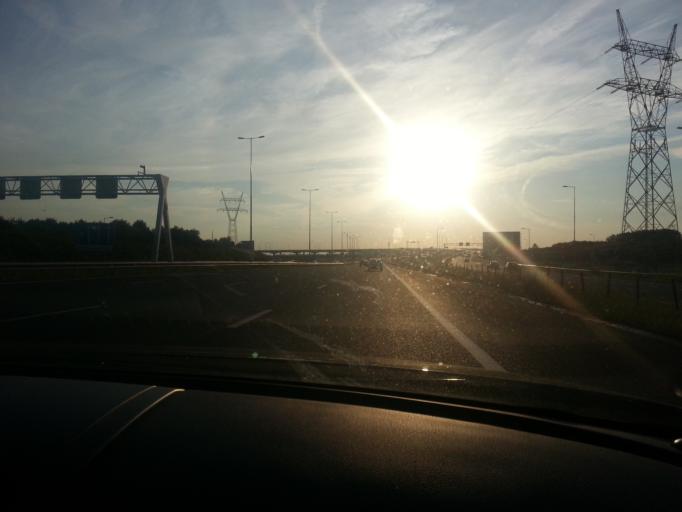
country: NL
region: South Holland
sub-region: Gemeente Barendrecht
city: Barendrecht
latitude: 51.8643
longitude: 4.5274
